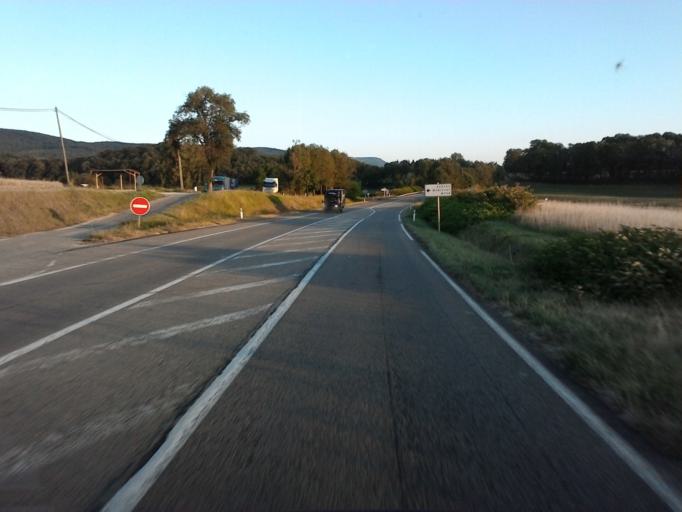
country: FR
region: Franche-Comte
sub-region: Departement du Doubs
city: Quingey
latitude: 47.0609
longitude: 5.8827
